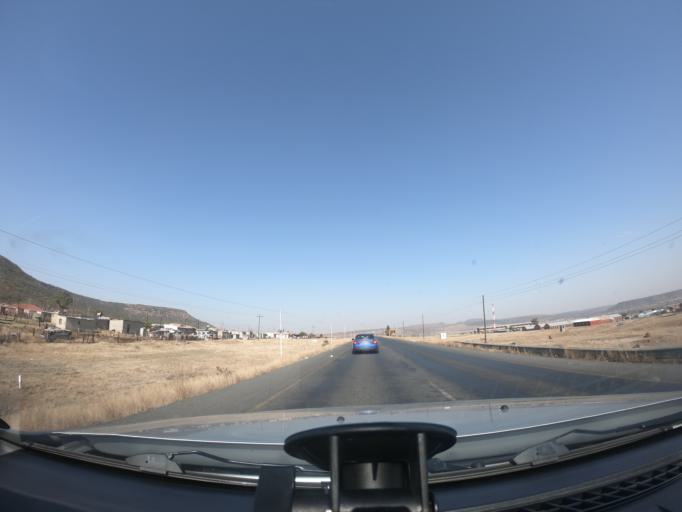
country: ZA
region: KwaZulu-Natal
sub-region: uThukela District Municipality
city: Ladysmith
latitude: -28.5691
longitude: 29.8348
